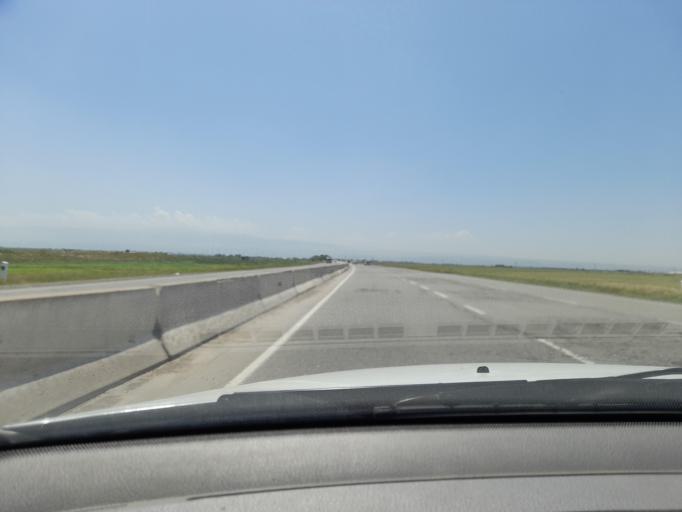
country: UZ
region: Jizzax
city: Paxtakor
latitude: 40.1982
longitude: 67.9754
